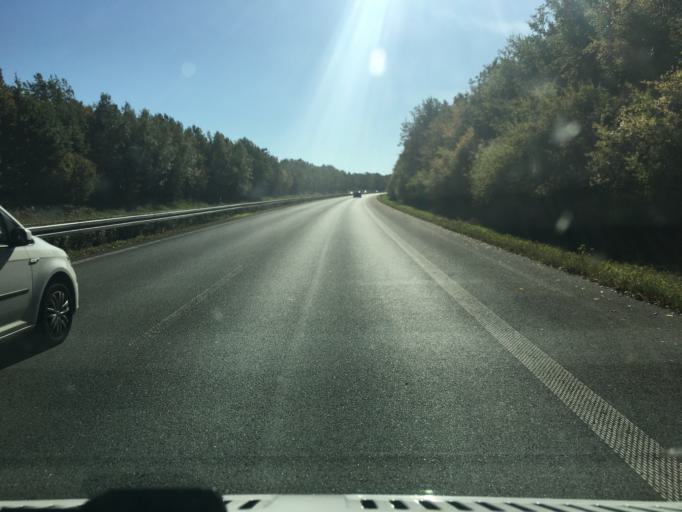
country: DE
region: Saxony
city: Dennheritz
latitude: 50.8058
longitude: 12.4545
